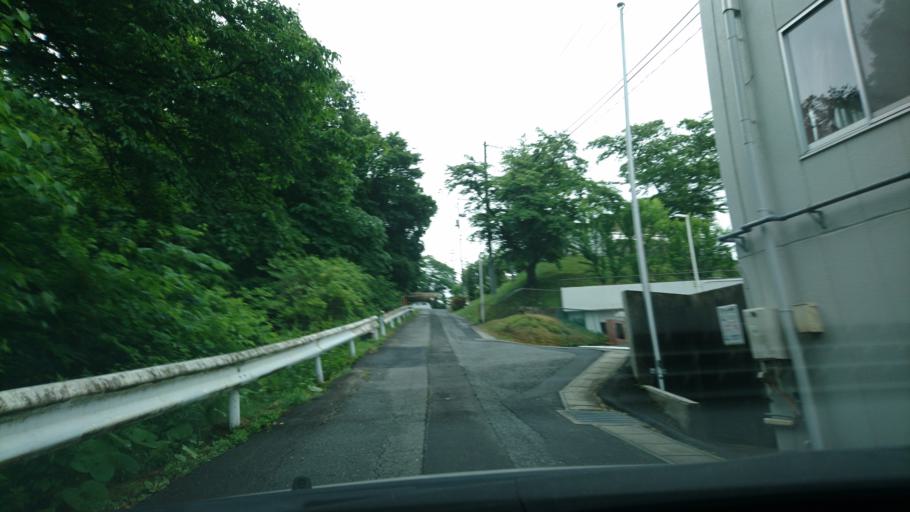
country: JP
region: Iwate
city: Ichinoseki
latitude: 38.8827
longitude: 141.1391
